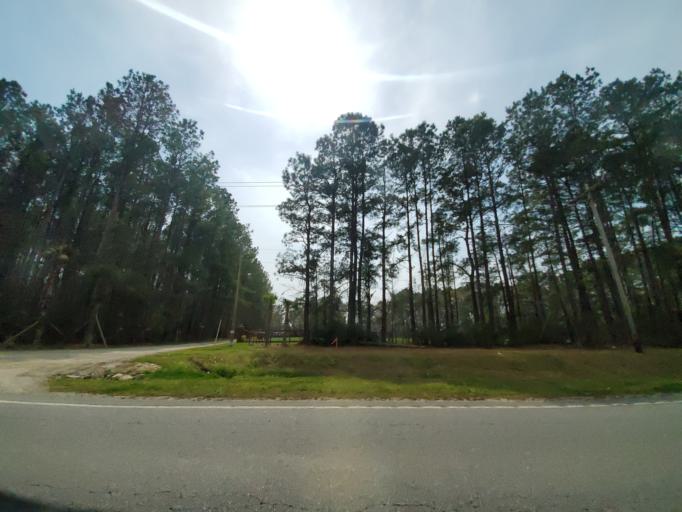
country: US
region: South Carolina
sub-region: Dorchester County
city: Ridgeville
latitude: 33.0002
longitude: -80.3200
